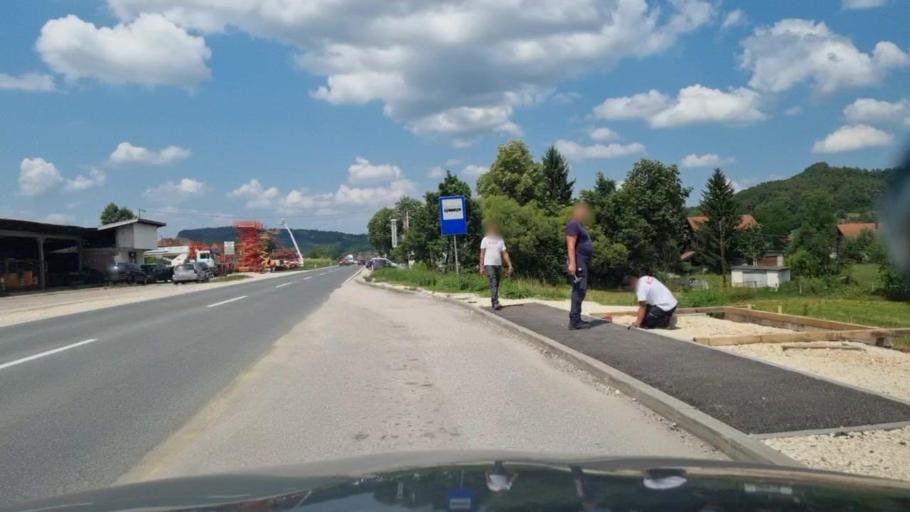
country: BA
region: Federation of Bosnia and Herzegovina
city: Mramor
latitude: 44.6316
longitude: 18.5589
